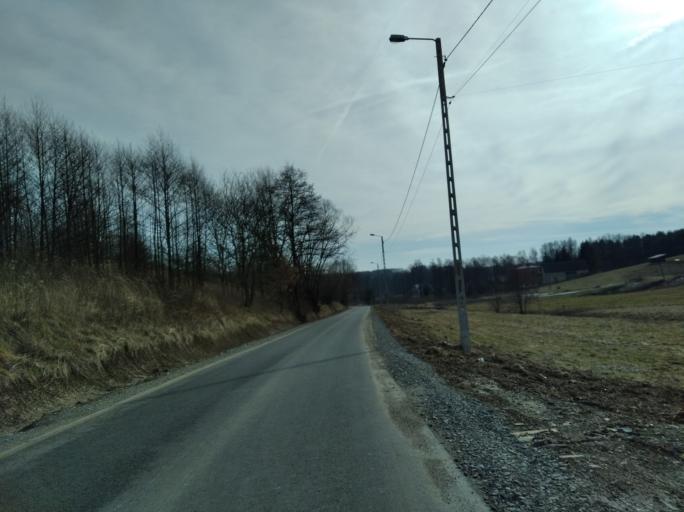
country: PL
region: Subcarpathian Voivodeship
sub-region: Powiat brzozowski
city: Jasienica Rosielna
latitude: 49.7622
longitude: 21.9455
